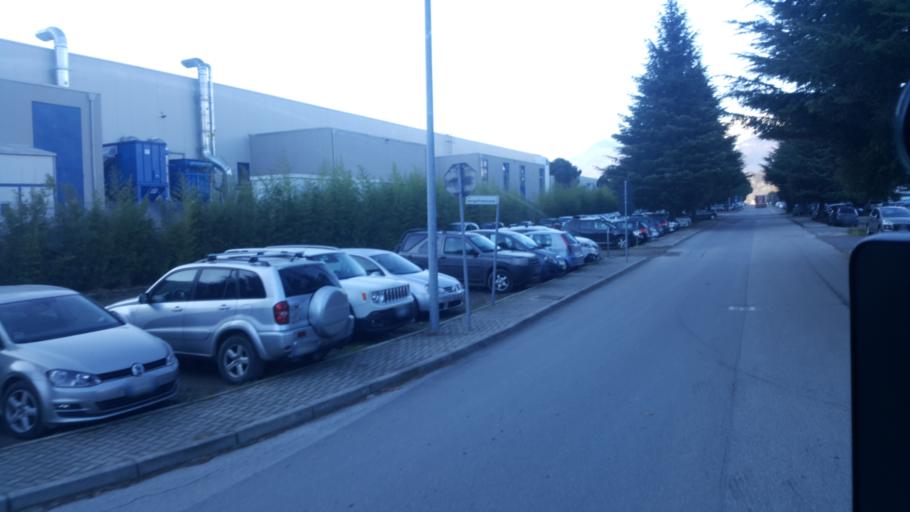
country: IT
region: Lombardy
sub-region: Provincia di Sondrio
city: Piantedo
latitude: 46.1407
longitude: 9.4044
